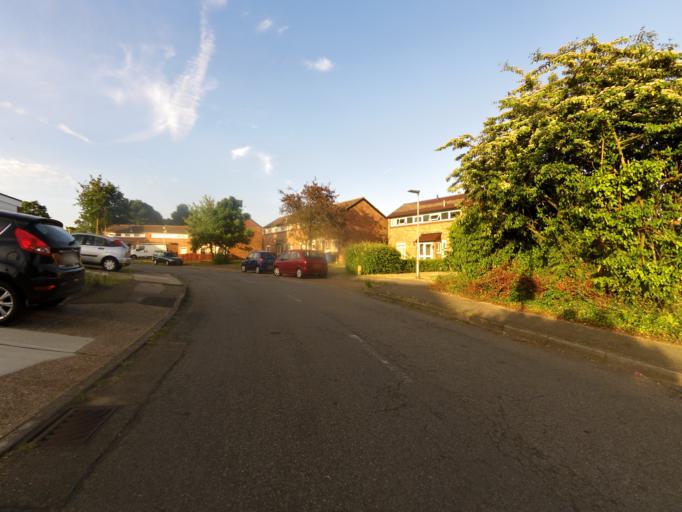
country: GB
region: England
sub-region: Suffolk
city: Ipswich
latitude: 52.0397
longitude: 1.1297
